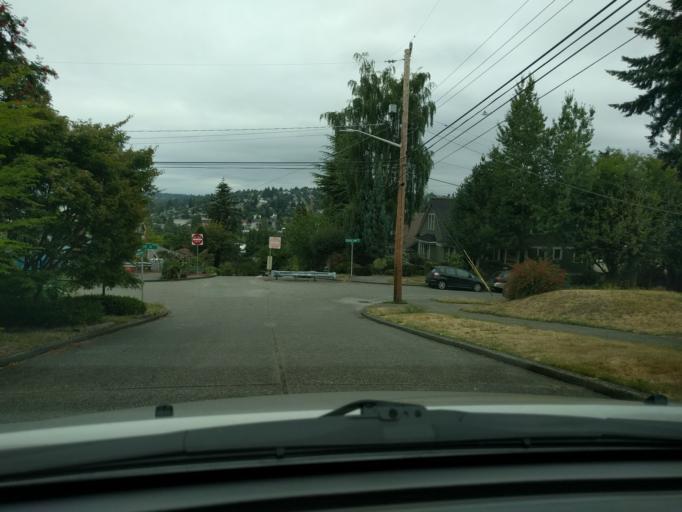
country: US
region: Washington
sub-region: King County
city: Seattle
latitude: 47.6455
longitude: -122.3569
